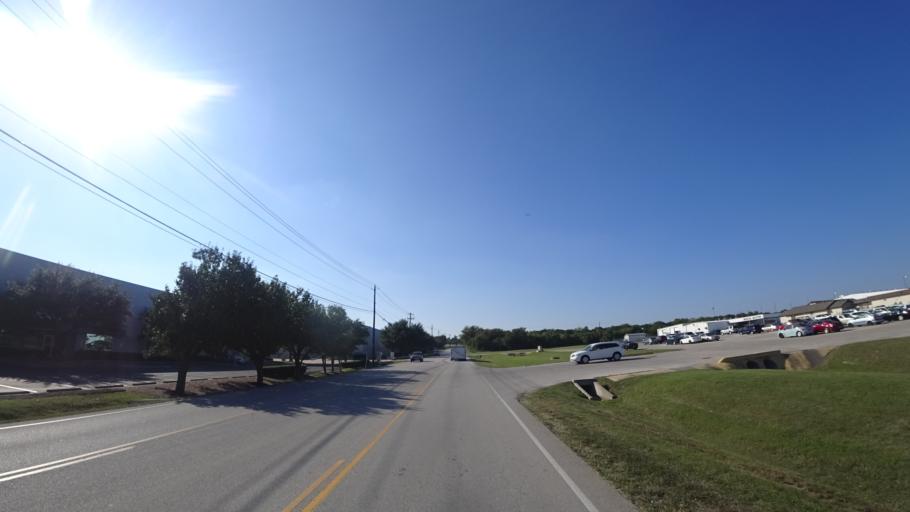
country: US
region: Texas
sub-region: Travis County
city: Wells Branch
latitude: 30.3435
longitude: -97.6665
